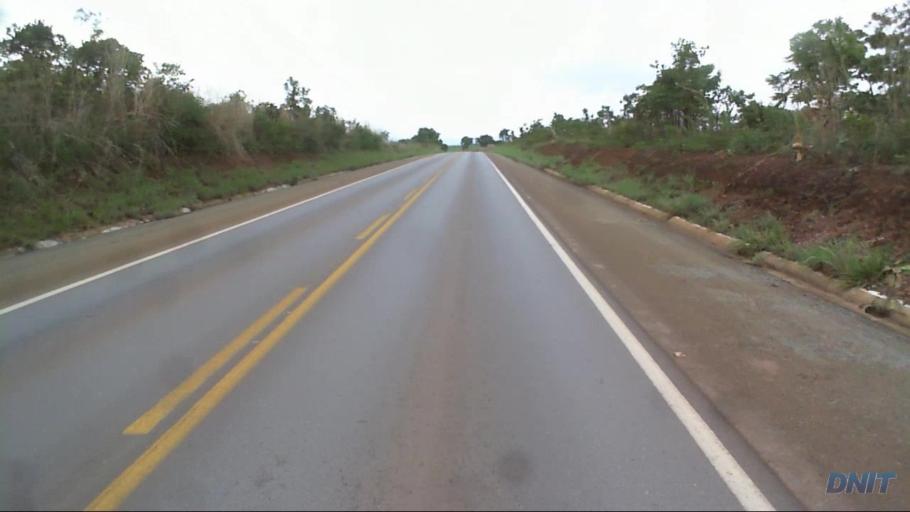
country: BR
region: Goias
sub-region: Barro Alto
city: Barro Alto
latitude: -14.7857
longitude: -49.0541
